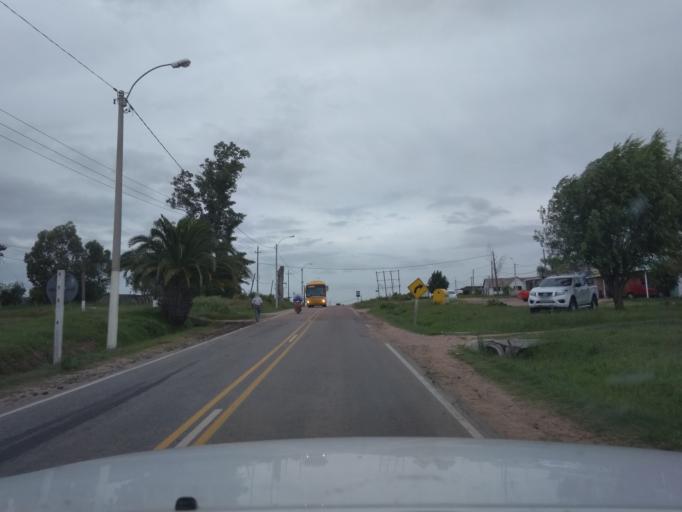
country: UY
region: Canelones
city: Tala
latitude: -34.3494
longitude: -55.7671
